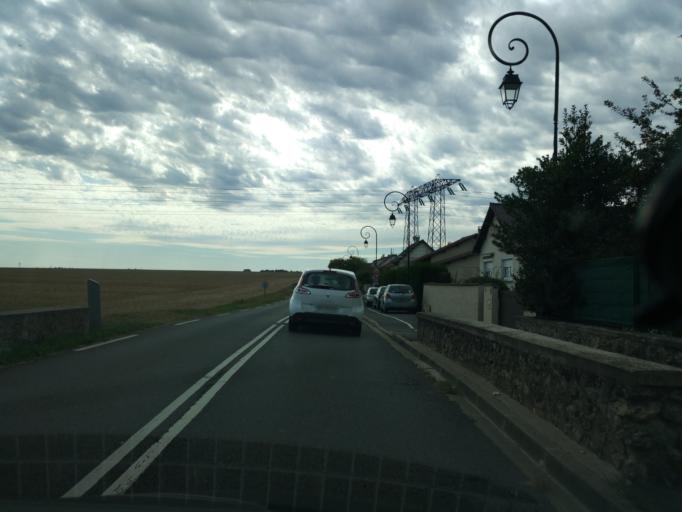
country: FR
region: Ile-de-France
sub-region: Departement de l'Essonne
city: Gometz-la-Ville
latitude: 48.6674
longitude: 2.1285
